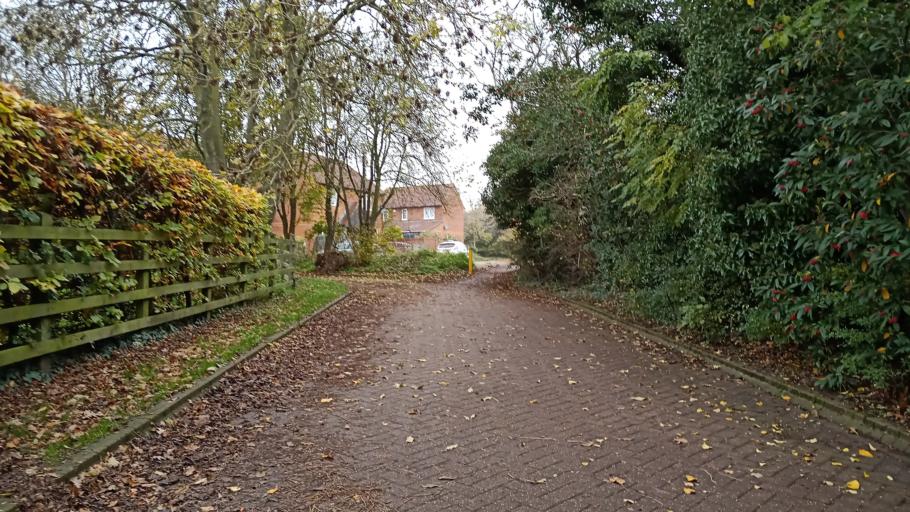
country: GB
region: England
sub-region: Milton Keynes
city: Shenley Church End
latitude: 52.0127
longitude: -0.7835
